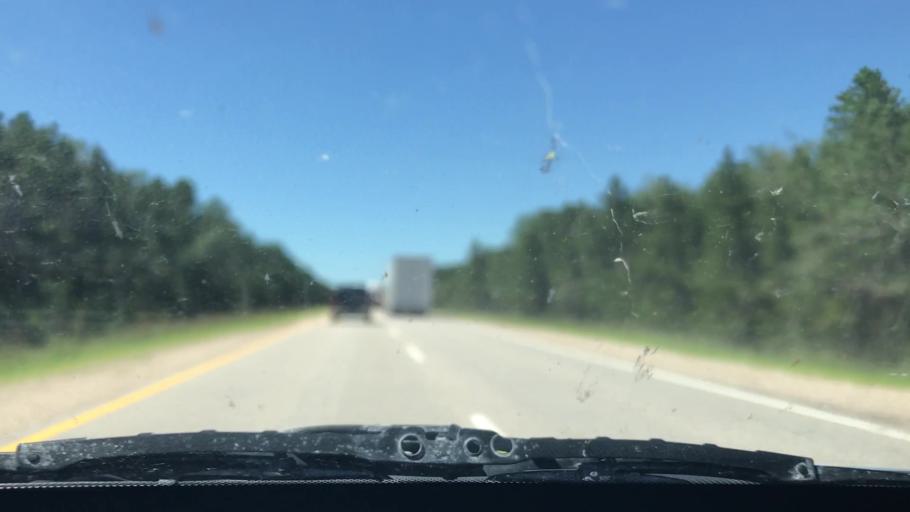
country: CA
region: Manitoba
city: La Broquerie
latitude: 49.6575
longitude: -96.1983
